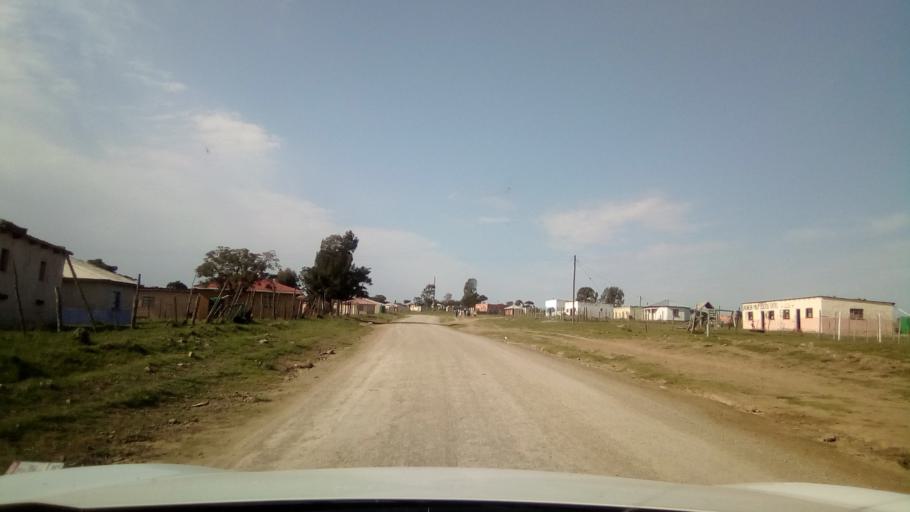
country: ZA
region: Eastern Cape
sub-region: Buffalo City Metropolitan Municipality
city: Bhisho
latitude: -32.9858
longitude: 27.2657
